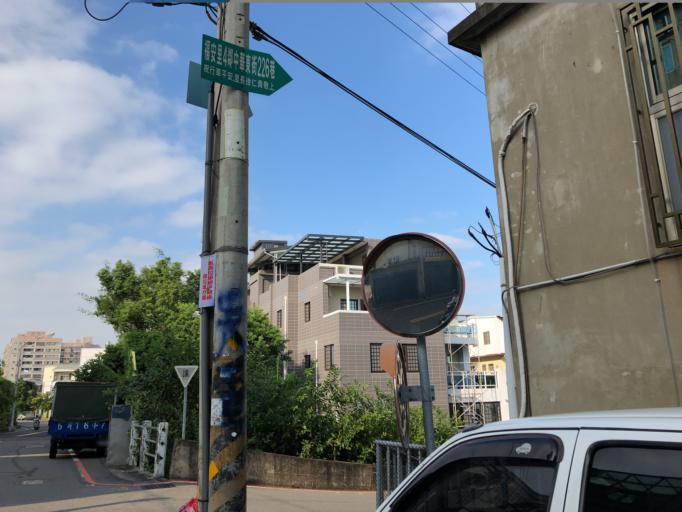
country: TW
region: Taiwan
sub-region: Miaoli
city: Miaoli
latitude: 24.5823
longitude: 120.8259
